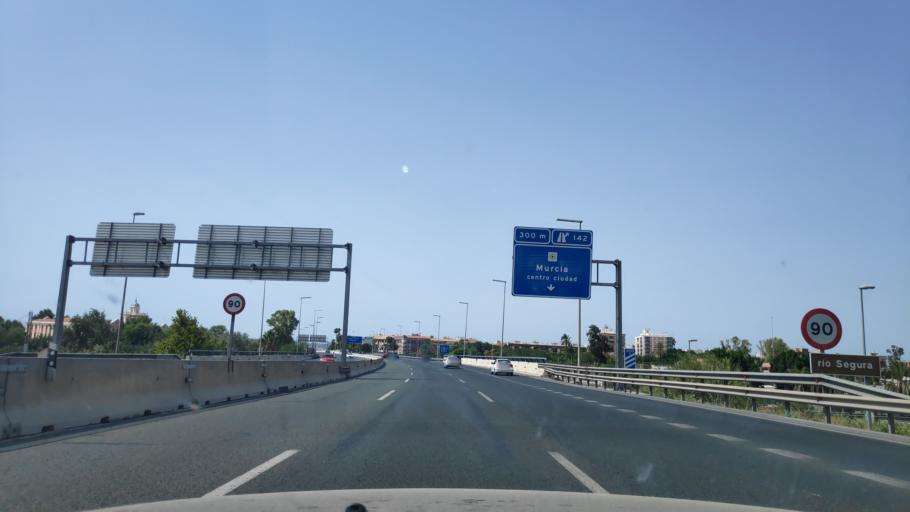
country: ES
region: Murcia
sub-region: Murcia
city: Murcia
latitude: 37.9783
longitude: -1.1368
